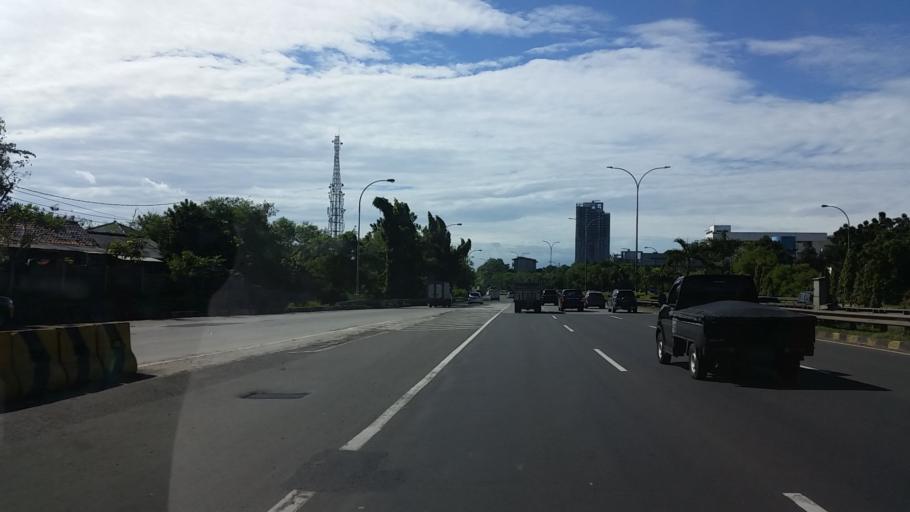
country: ID
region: Banten
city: South Tangerang
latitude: -6.2650
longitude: 106.7679
